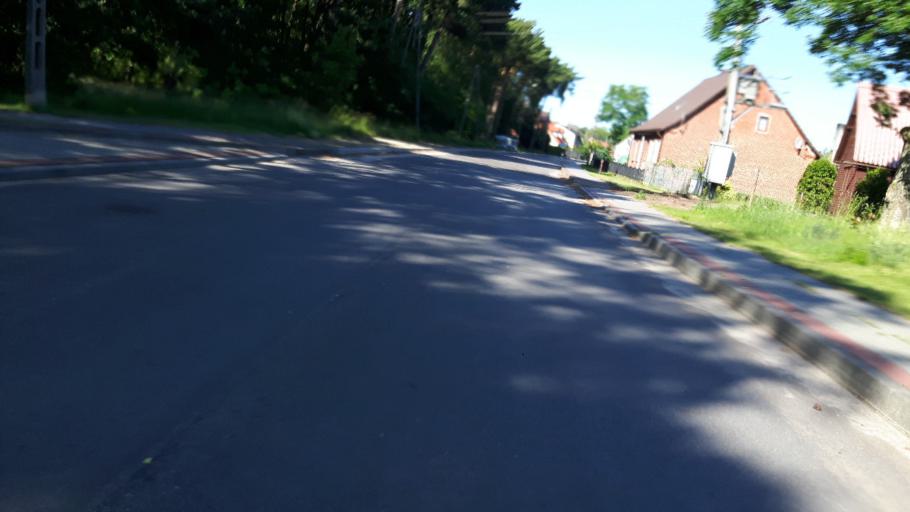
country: PL
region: Pomeranian Voivodeship
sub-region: Powiat leborski
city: Leba
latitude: 54.7215
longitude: 17.5273
